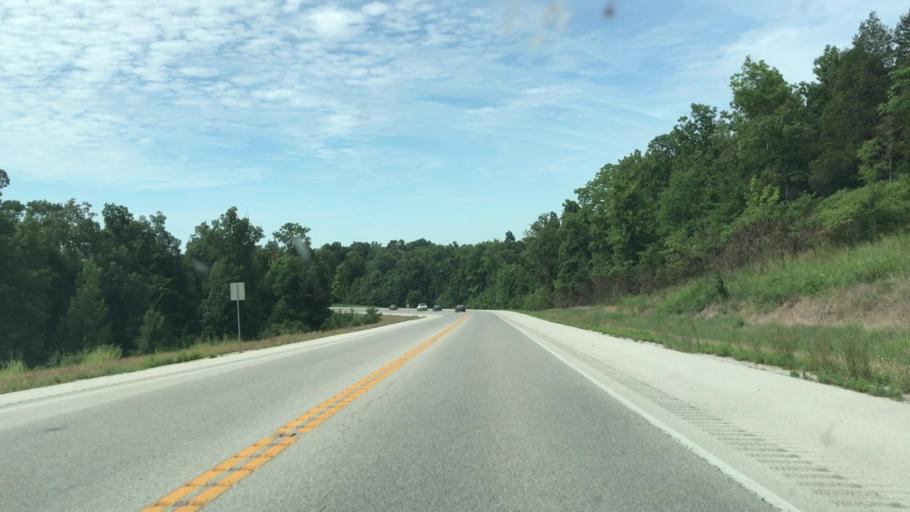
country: US
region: Kentucky
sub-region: Edmonson County
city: Brownsville
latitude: 37.0966
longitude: -86.2324
